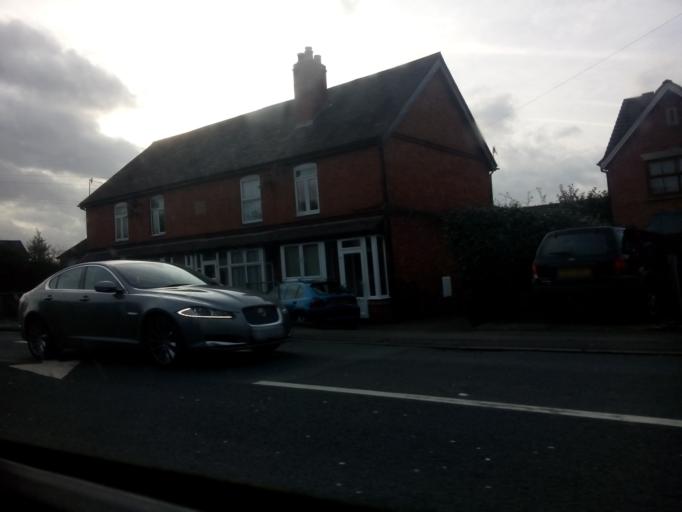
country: GB
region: England
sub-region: Worcestershire
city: Bromsgrove
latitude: 52.3635
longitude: -2.0468
